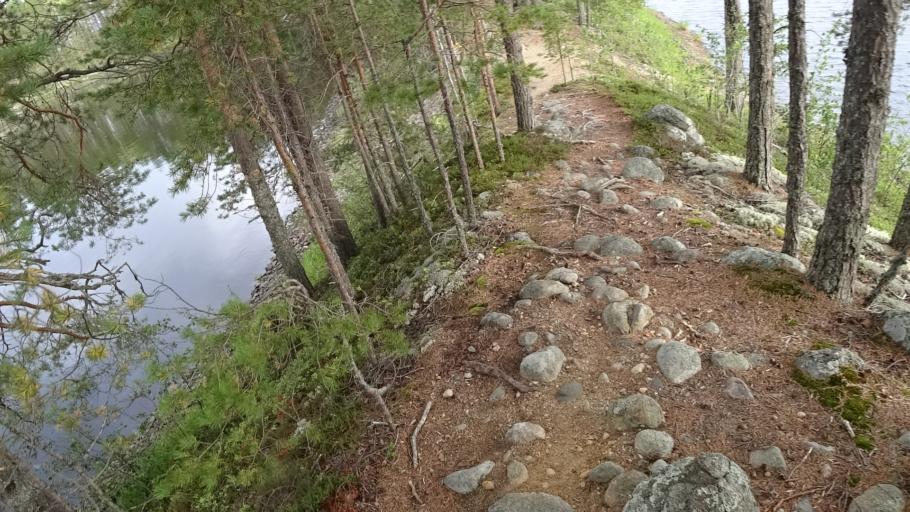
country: FI
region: North Karelia
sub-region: Joensuu
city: Ilomantsi
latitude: 62.5734
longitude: 31.1731
